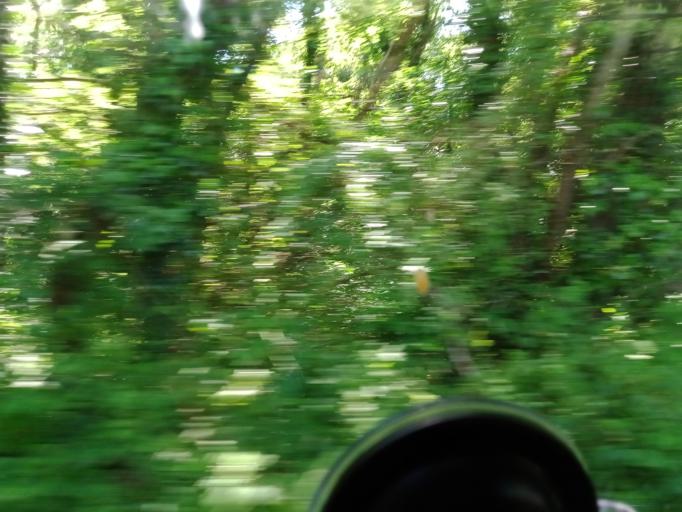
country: IE
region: Leinster
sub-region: Kilkenny
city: Thomastown
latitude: 52.5532
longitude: -7.0909
